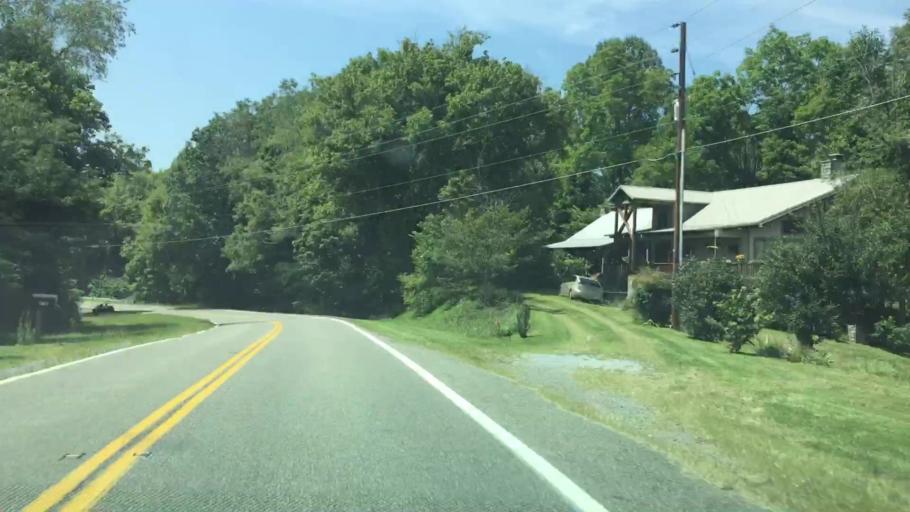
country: US
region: Virginia
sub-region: Washington County
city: Abingdon
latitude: 36.6068
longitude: -82.0340
